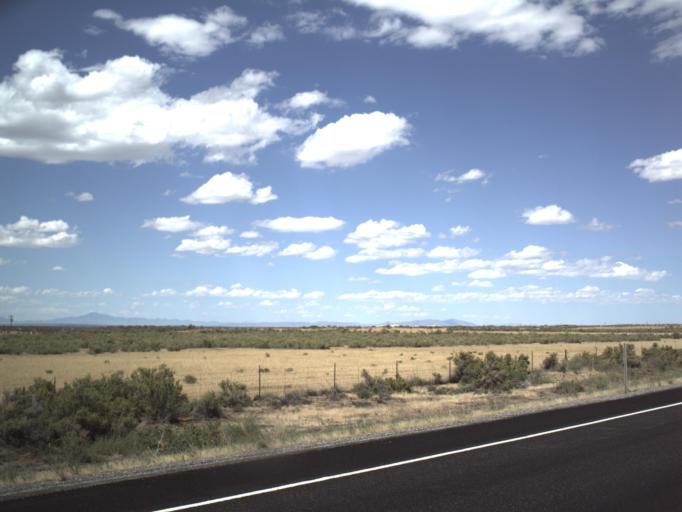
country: US
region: Utah
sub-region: Millard County
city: Fillmore
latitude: 39.1222
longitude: -112.3573
